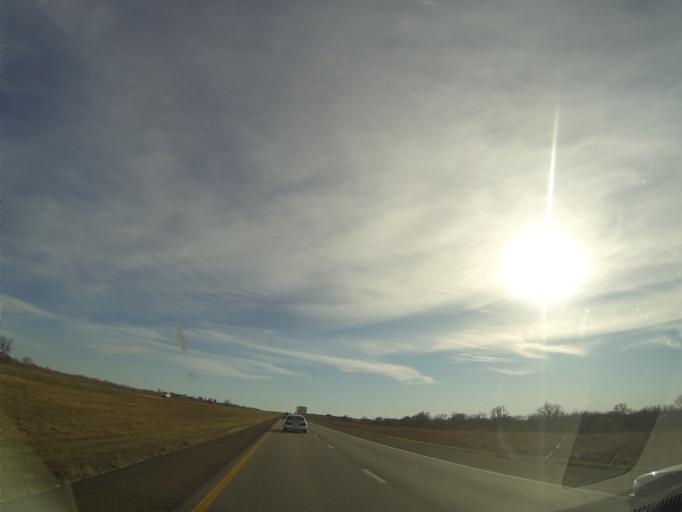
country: US
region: Kansas
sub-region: Ottawa County
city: Minneapolis
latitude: 38.9967
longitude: -97.6397
